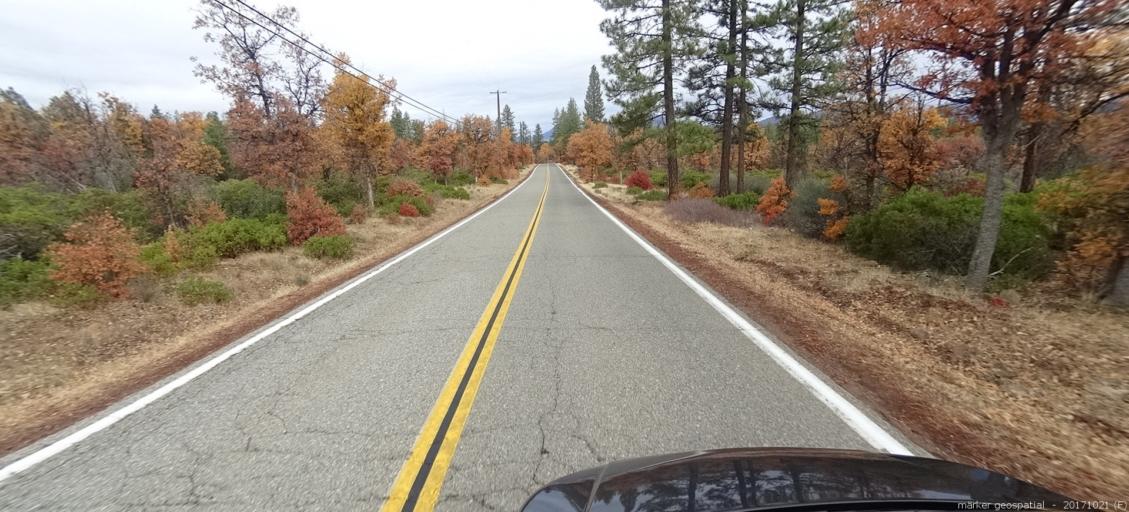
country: US
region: California
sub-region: Shasta County
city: Burney
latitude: 40.9253
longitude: -121.5655
